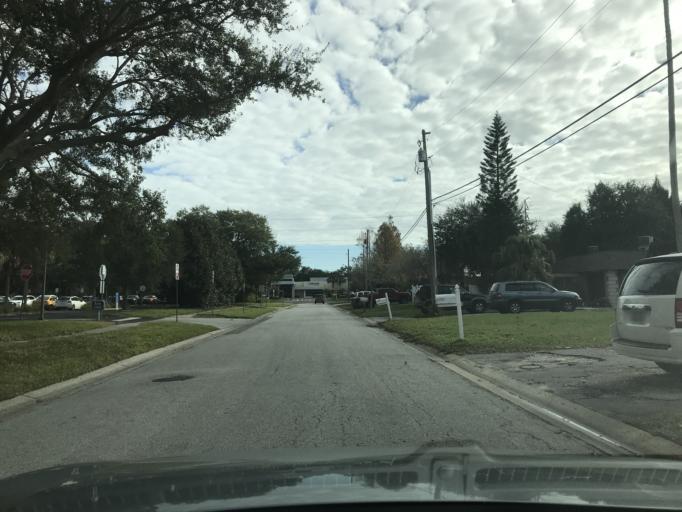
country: US
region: Florida
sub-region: Pinellas County
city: Largo
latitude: 27.9183
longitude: -82.7764
